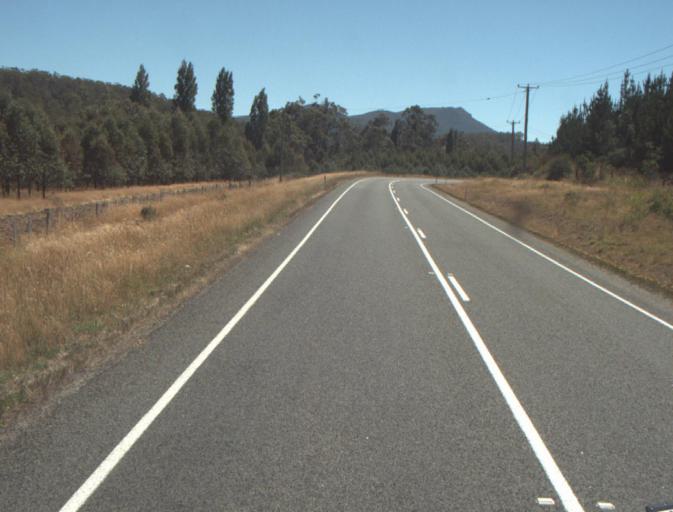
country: AU
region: Tasmania
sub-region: Launceston
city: Newstead
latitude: -41.3803
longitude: 147.3114
